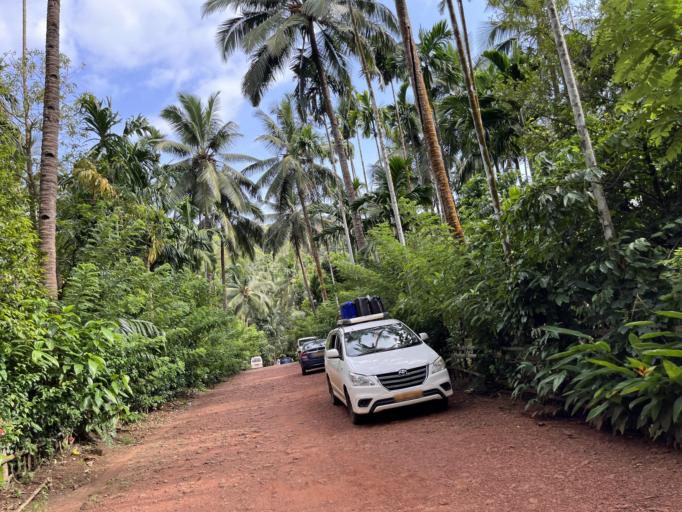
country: IN
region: Goa
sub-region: North Goa
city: Ponda
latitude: 15.4091
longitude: 74.0242
